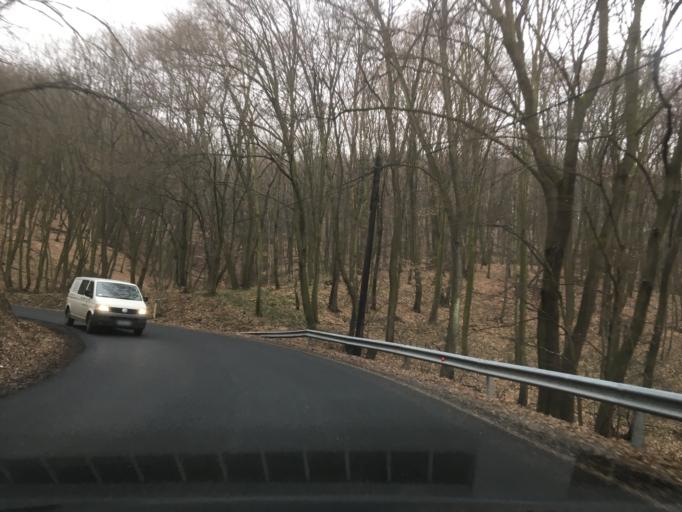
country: HU
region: Komarom-Esztergom
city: Kesztolc
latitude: 47.7378
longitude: 18.8126
